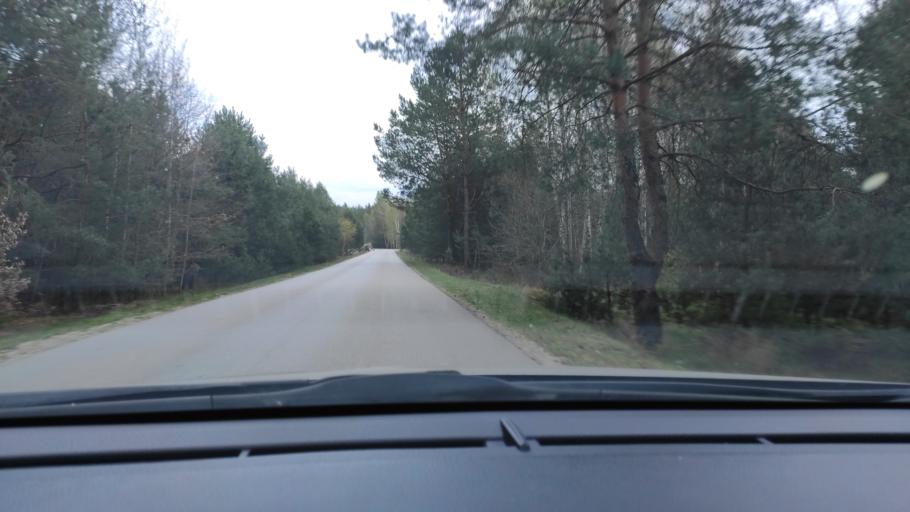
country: PL
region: Masovian Voivodeship
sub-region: Powiat radomski
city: Pionki
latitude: 51.5425
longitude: 21.3842
